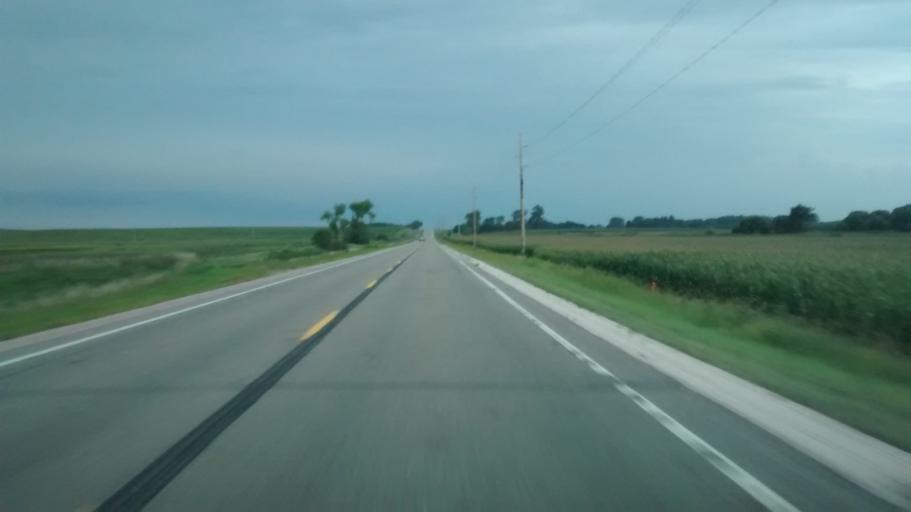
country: US
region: Iowa
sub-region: Woodbury County
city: Moville
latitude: 42.5244
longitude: -96.0429
